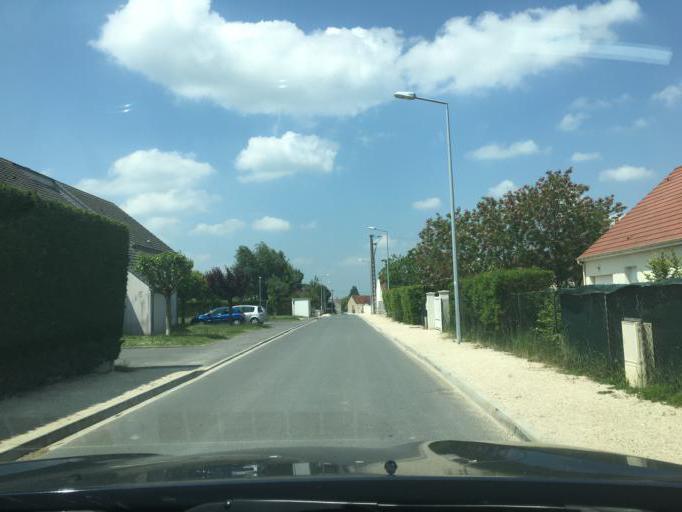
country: FR
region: Centre
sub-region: Departement du Loiret
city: Trainou
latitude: 47.9787
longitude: 2.1073
